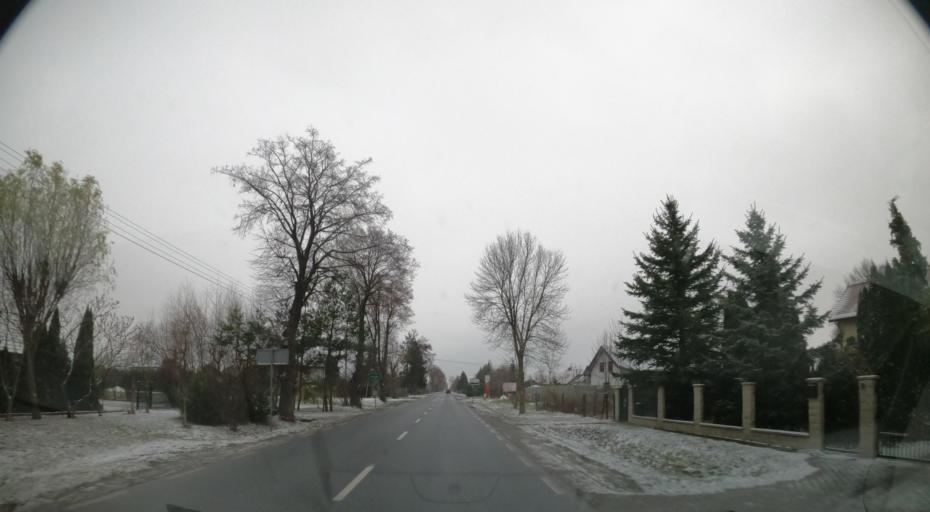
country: PL
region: Masovian Voivodeship
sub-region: Powiat plocki
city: Maszewo Duze
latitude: 52.5630
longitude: 19.6350
